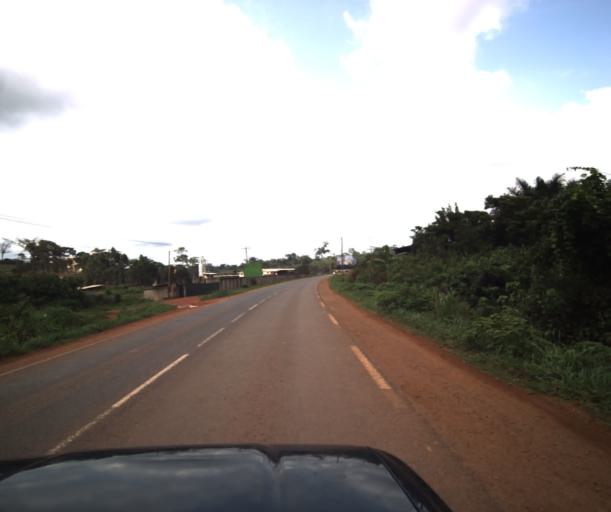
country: CM
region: Centre
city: Mbankomo
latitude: 3.7861
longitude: 11.4688
